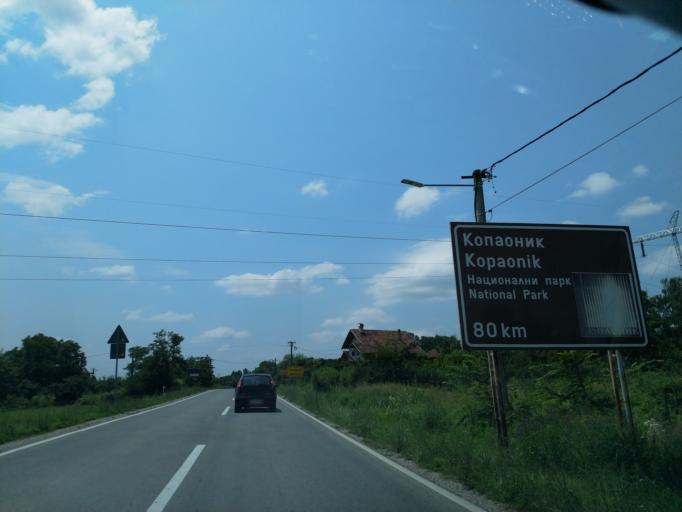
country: RS
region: Central Serbia
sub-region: Rasinski Okrug
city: Krusevac
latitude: 43.5306
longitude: 21.3185
